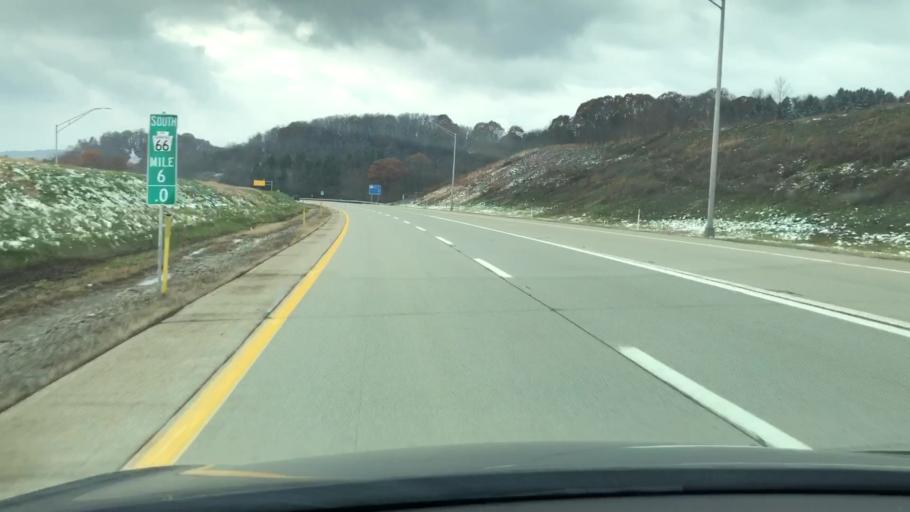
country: US
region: Pennsylvania
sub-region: Westmoreland County
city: Jeannette
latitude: 40.3057
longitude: -79.6012
